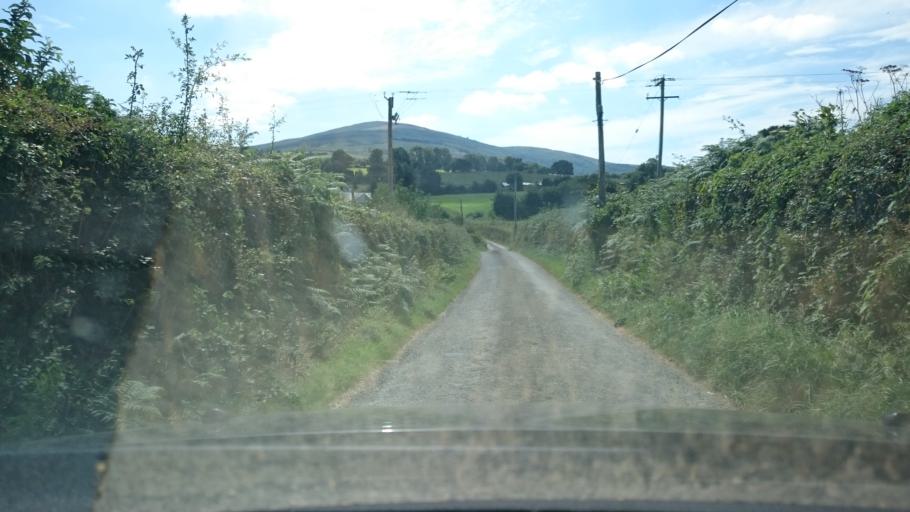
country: IE
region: Leinster
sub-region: Kilkenny
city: Graiguenamanagh
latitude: 52.5392
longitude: -6.9655
